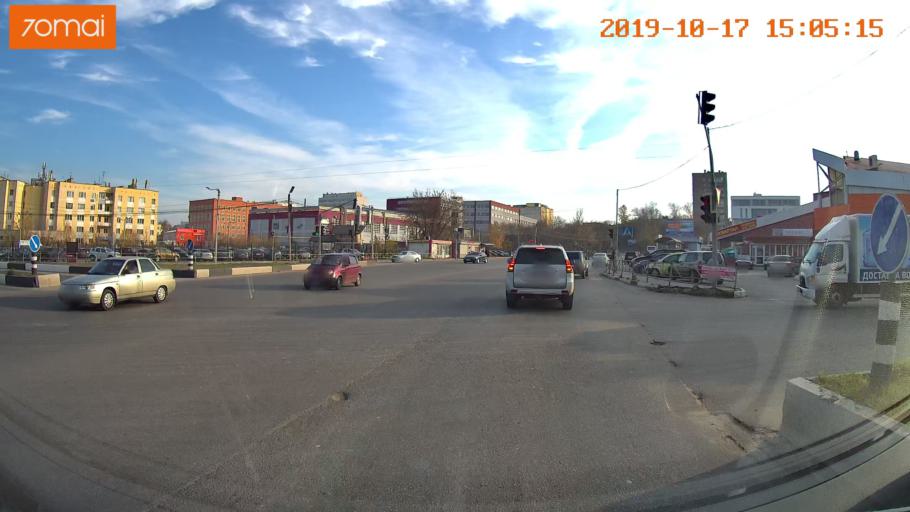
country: RU
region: Rjazan
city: Ryazan'
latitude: 54.6371
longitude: 39.7228
